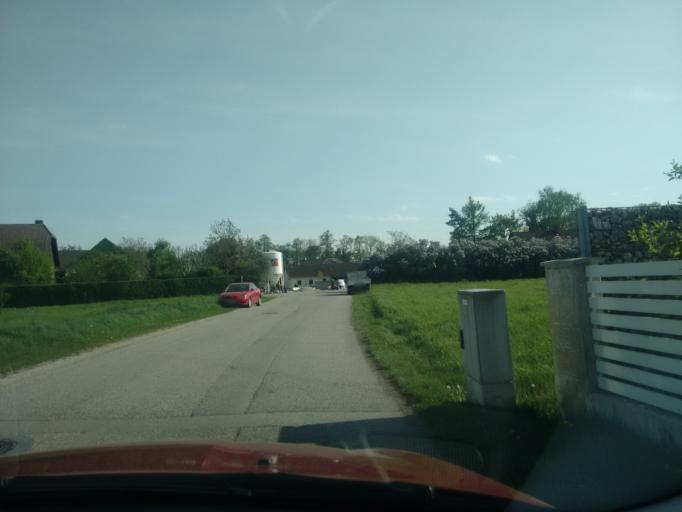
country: AT
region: Upper Austria
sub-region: Wels-Land
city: Marchtrenk
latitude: 48.1831
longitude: 14.0925
